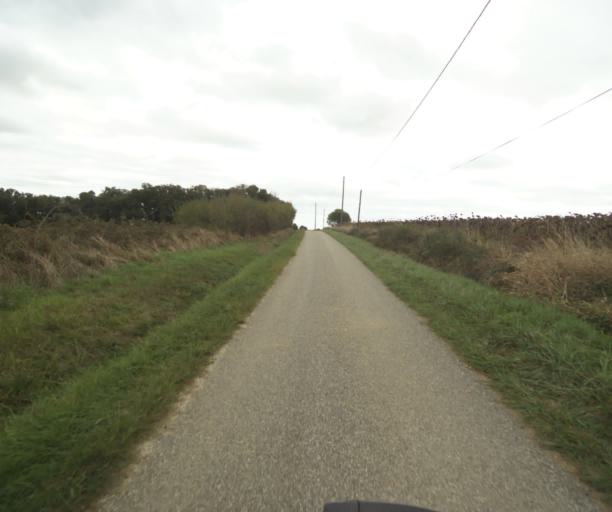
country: FR
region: Midi-Pyrenees
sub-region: Departement du Tarn-et-Garonne
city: Beaumont-de-Lomagne
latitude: 43.8561
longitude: 1.0618
